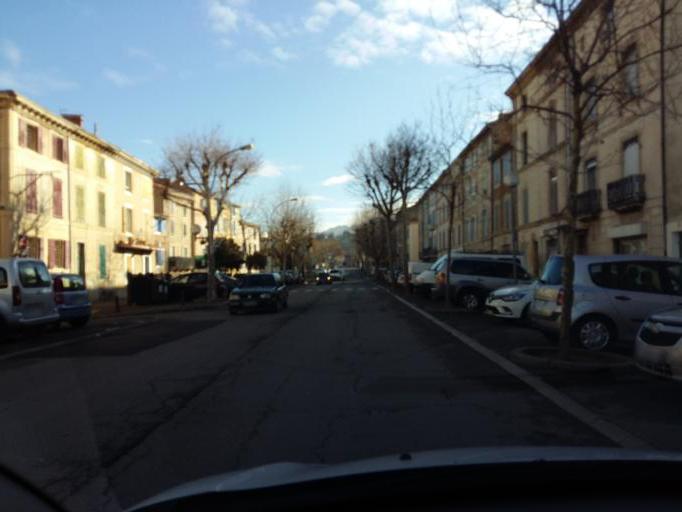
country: FR
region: Provence-Alpes-Cote d'Azur
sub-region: Departement du Vaucluse
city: Apt
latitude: 43.8741
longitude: 5.3960
